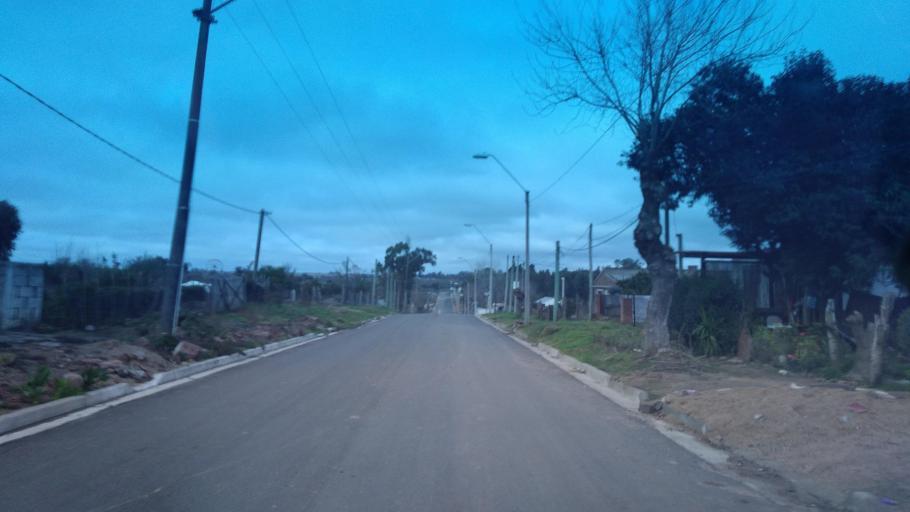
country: UY
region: Canelones
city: Tala
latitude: -34.2008
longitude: -55.7404
